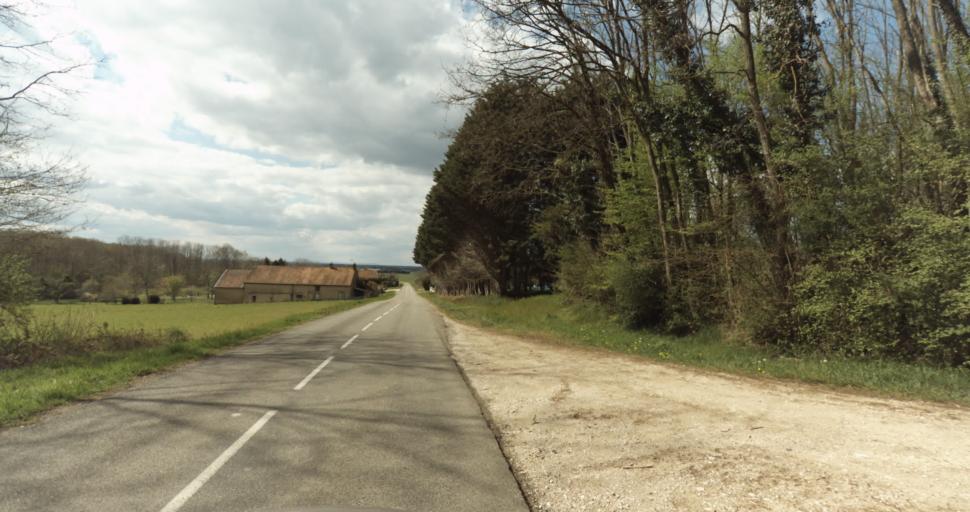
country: FR
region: Bourgogne
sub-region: Departement de la Cote-d'Or
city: Auxonne
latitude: 47.1935
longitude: 5.4316
